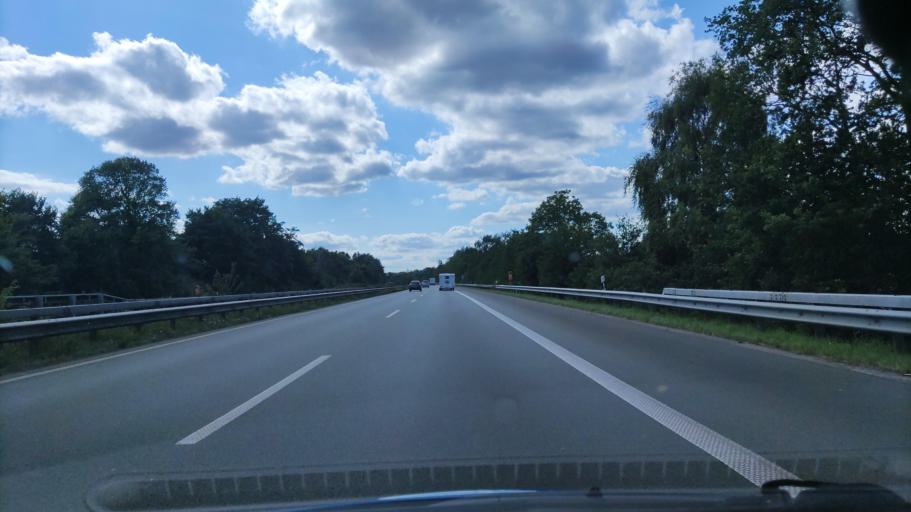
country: DE
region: Lower Saxony
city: Hatten
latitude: 53.0595
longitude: 8.4356
